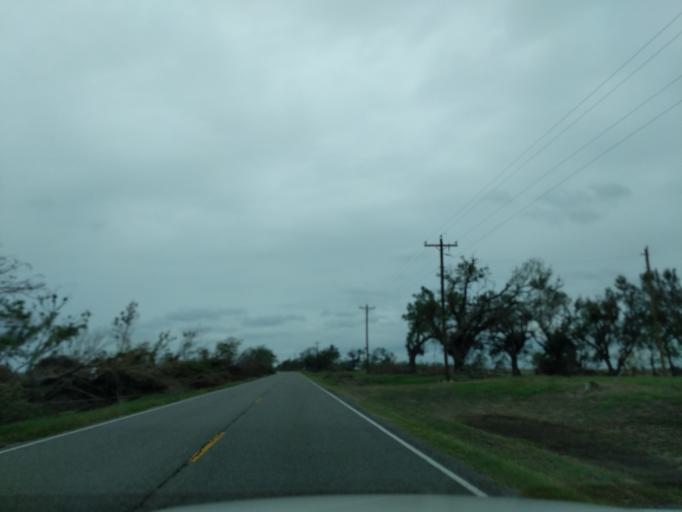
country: US
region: Louisiana
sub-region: Cameron Parish
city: Cameron
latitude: 29.7867
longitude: -93.1349
